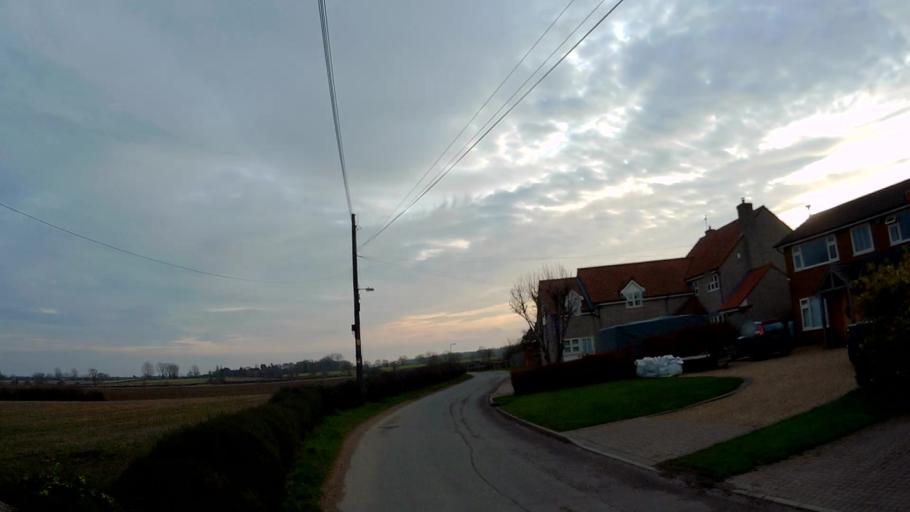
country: GB
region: England
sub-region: Lincolnshire
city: Bourne
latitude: 52.8118
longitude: -0.3984
